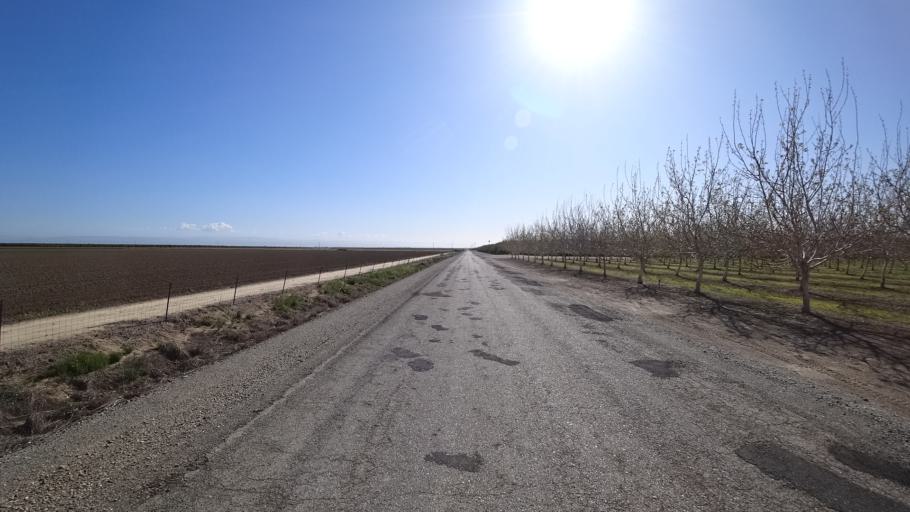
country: US
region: California
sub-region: Glenn County
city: Hamilton City
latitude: 39.6782
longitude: -122.0475
